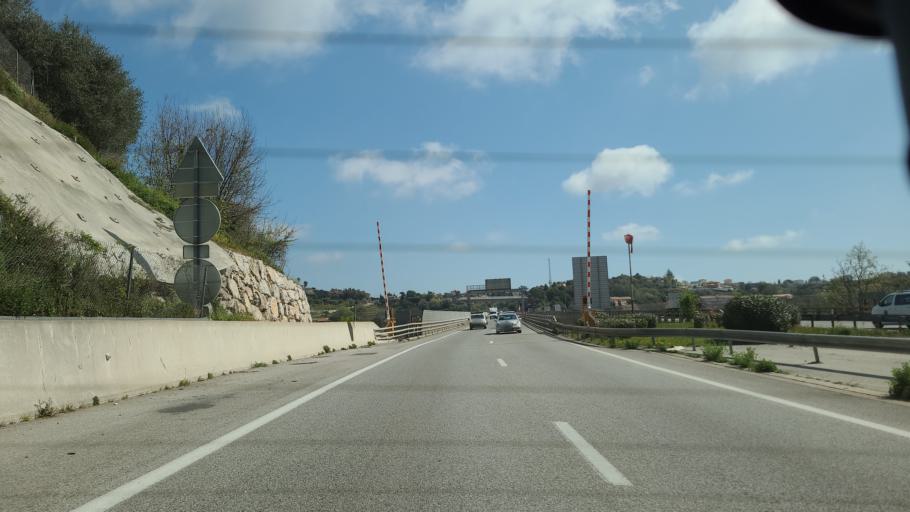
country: FR
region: Provence-Alpes-Cote d'Azur
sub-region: Departement des Alpes-Maritimes
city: Colomars
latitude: 43.7221
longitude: 7.2190
